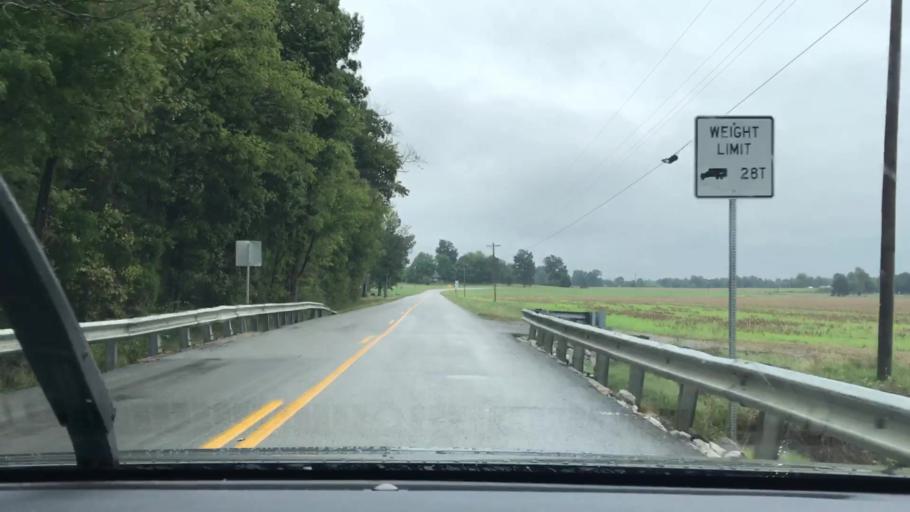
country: US
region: Kentucky
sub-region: McLean County
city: Calhoun
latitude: 37.4721
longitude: -87.2377
